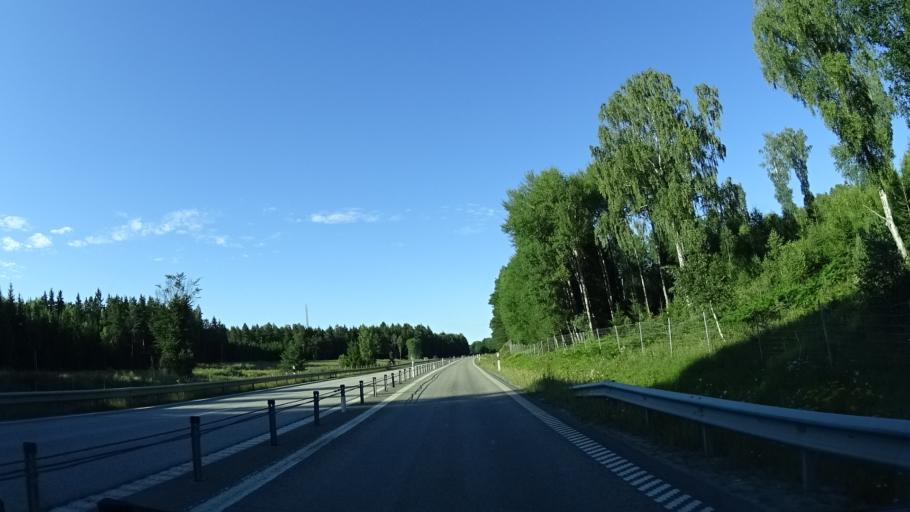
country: SE
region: Stockholm
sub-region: Vallentuna Kommun
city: Vallentuna
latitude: 59.5201
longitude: 18.1817
